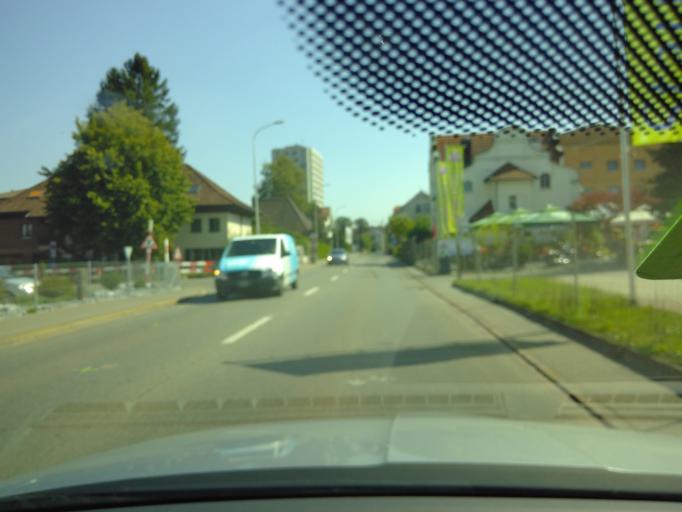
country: CH
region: Aargau
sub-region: Bezirk Kulm
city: Reinach
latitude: 47.2604
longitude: 8.1783
